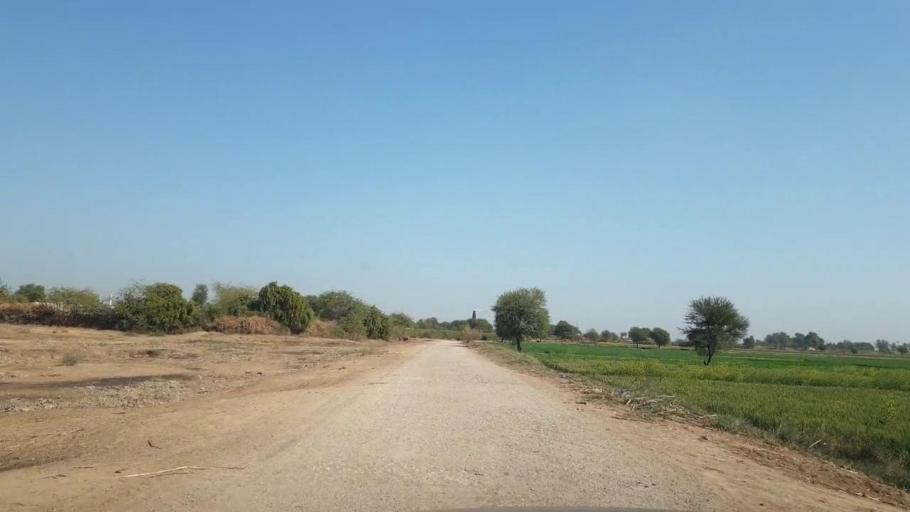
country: PK
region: Sindh
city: Tando Adam
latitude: 25.6554
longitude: 68.6799
